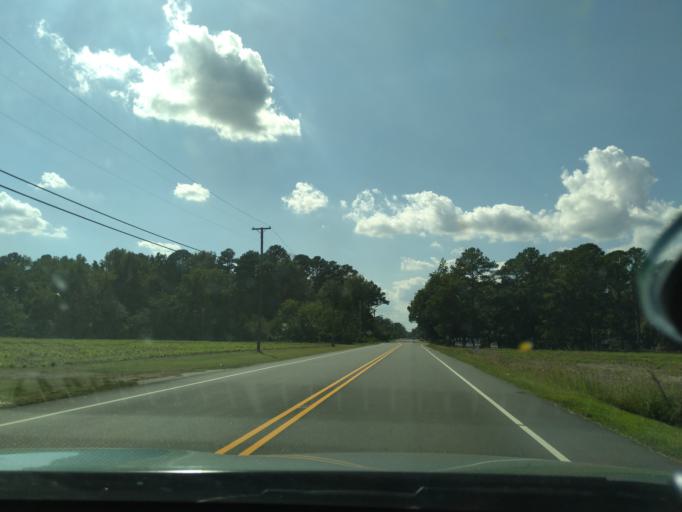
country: US
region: North Carolina
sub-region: Martin County
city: Robersonville
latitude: 35.8268
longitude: -77.2459
